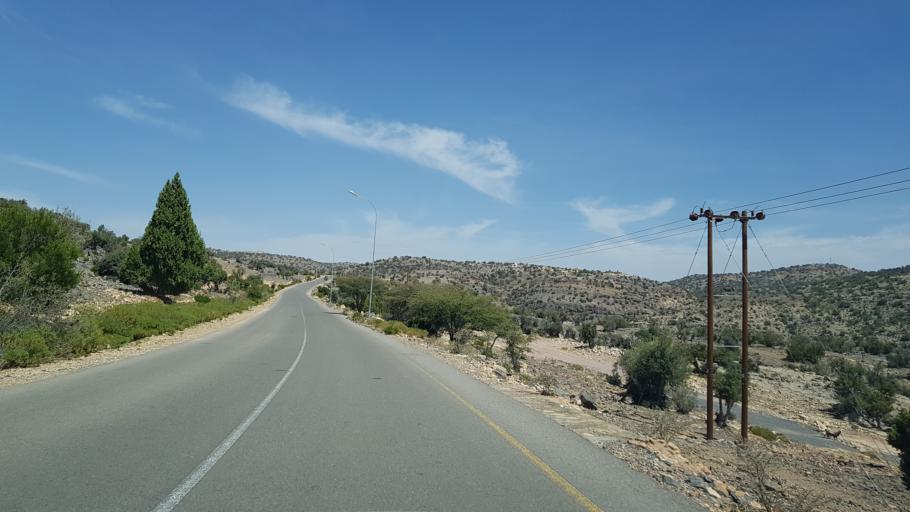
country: OM
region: Al Batinah
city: Bayt al `Awabi
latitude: 23.1384
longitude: 57.5750
